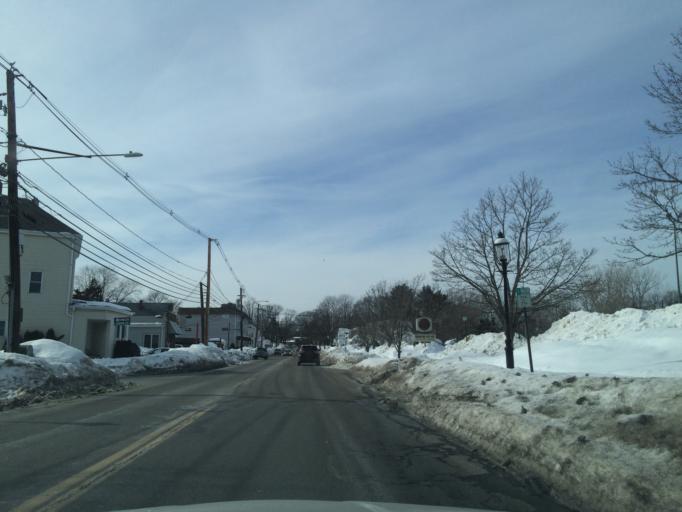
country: US
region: Massachusetts
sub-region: Middlesex County
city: Watertown
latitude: 42.3649
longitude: -71.1993
